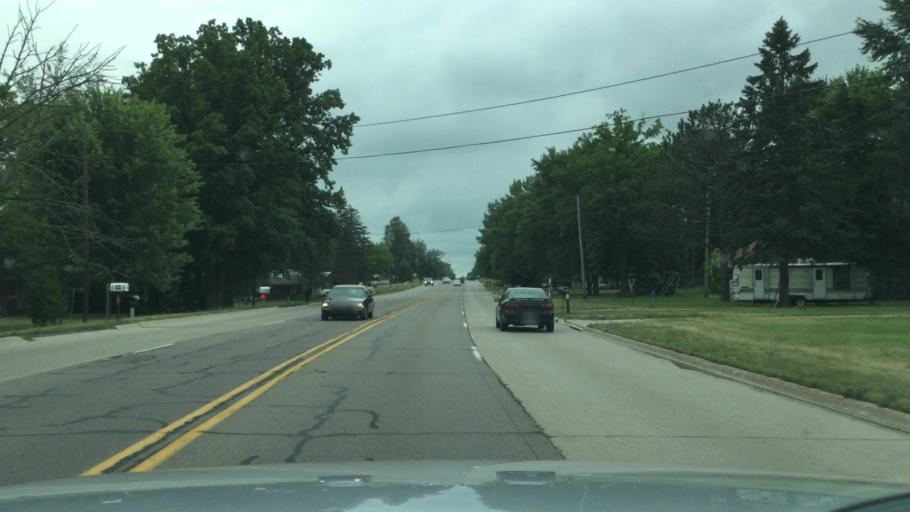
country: US
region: Michigan
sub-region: Genesee County
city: Burton
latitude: 43.0541
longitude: -83.6161
